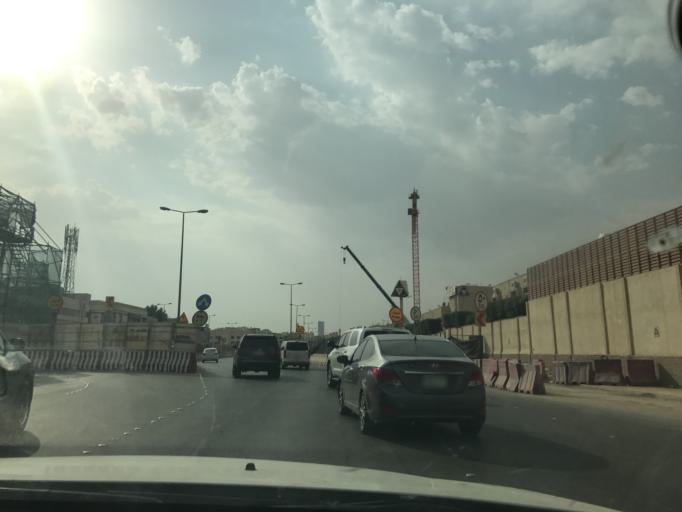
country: SA
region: Ar Riyad
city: Riyadh
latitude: 24.7122
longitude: 46.7022
